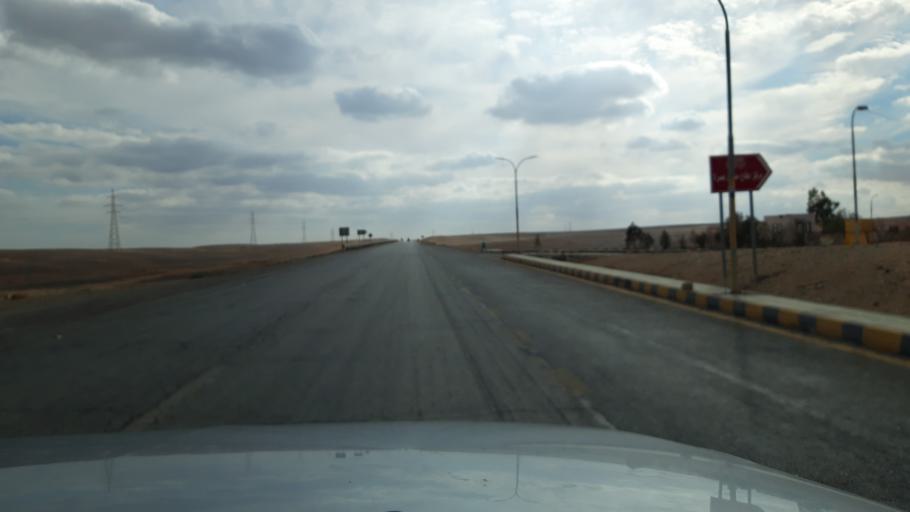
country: JO
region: Amman
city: Al Azraq ash Shamali
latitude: 31.7522
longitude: 36.5439
